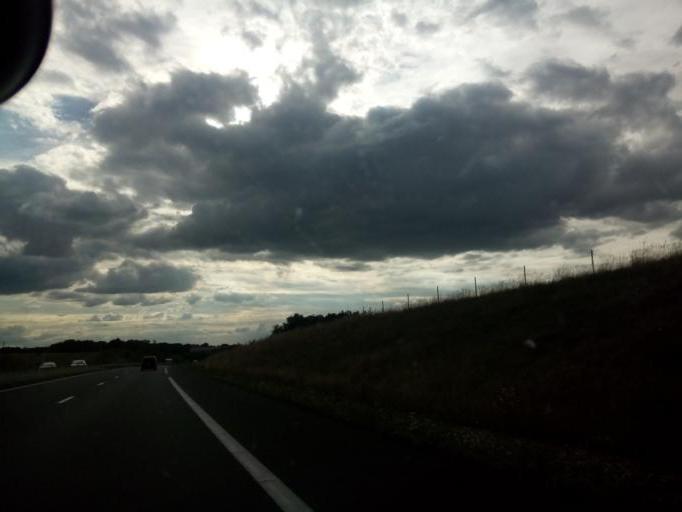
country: FR
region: Centre
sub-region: Departement d'Indre-et-Loire
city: Civray-de-Touraine
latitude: 47.2864
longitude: 1.0756
